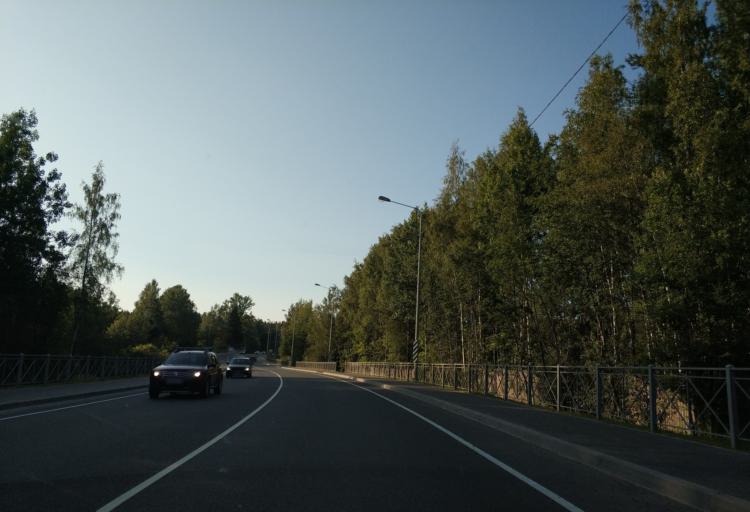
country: RU
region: Leningrad
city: Sapernoye
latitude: 60.7014
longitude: 29.9721
